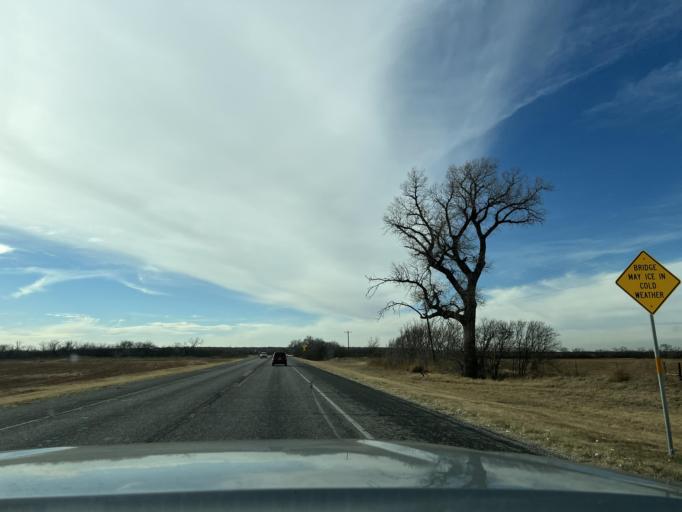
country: US
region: Texas
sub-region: Fisher County
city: Roby
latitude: 32.7612
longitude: -100.3042
